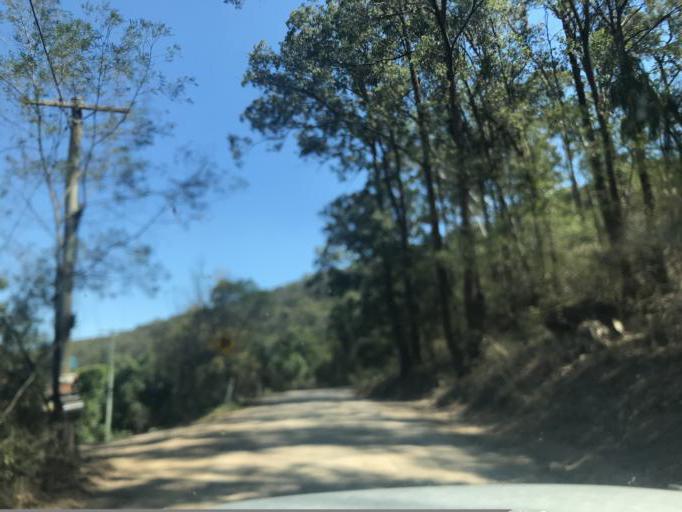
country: AU
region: New South Wales
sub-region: Hawkesbury
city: Pitt Town
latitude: -33.4200
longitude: 150.8980
